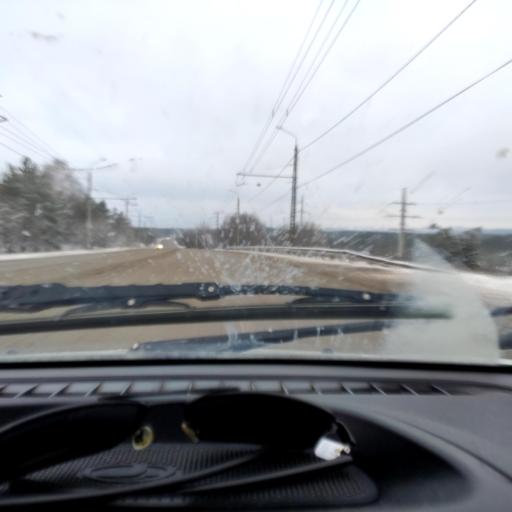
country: RU
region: Samara
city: Zhigulevsk
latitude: 53.5076
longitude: 49.5185
